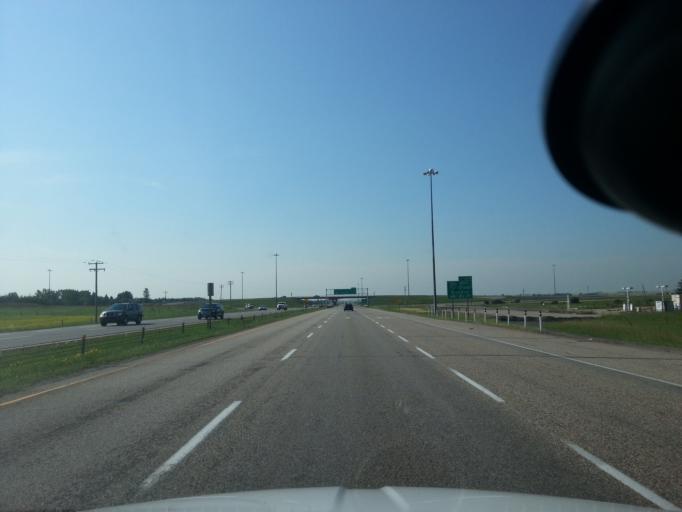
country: CA
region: Alberta
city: Olds
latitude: 51.7988
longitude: -114.0256
